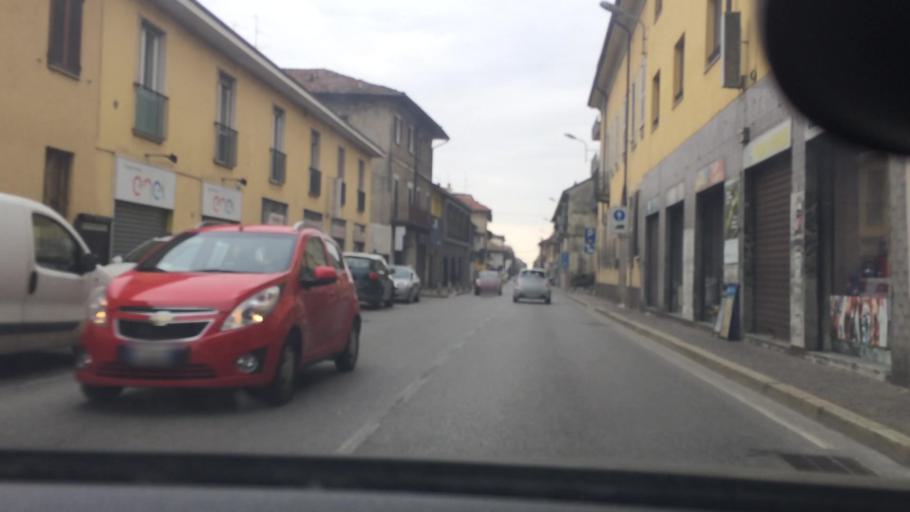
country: IT
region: Lombardy
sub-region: Provincia di Monza e Brianza
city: Barlassina
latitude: 45.6570
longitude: 9.1285
